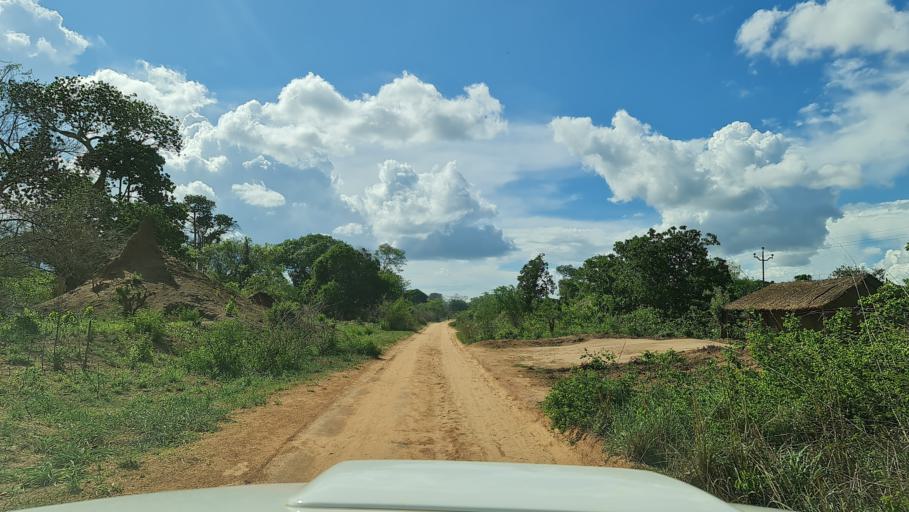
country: MZ
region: Nampula
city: Ilha de Mocambique
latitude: -15.4359
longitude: 40.2787
